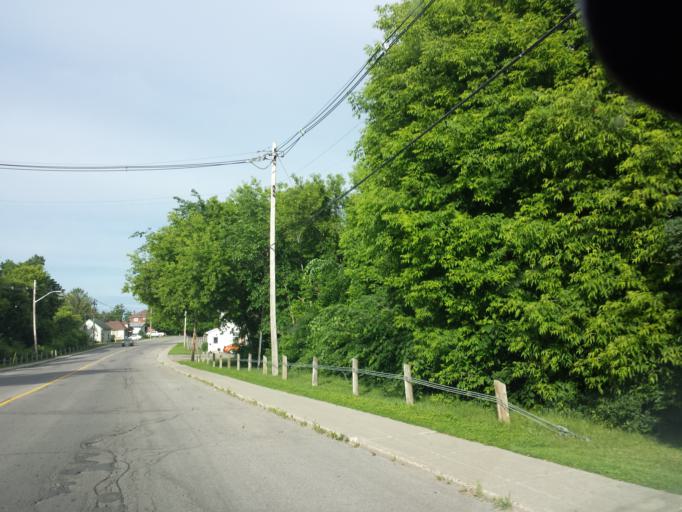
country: CA
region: Ontario
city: Renfrew
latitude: 45.4732
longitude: -76.6930
